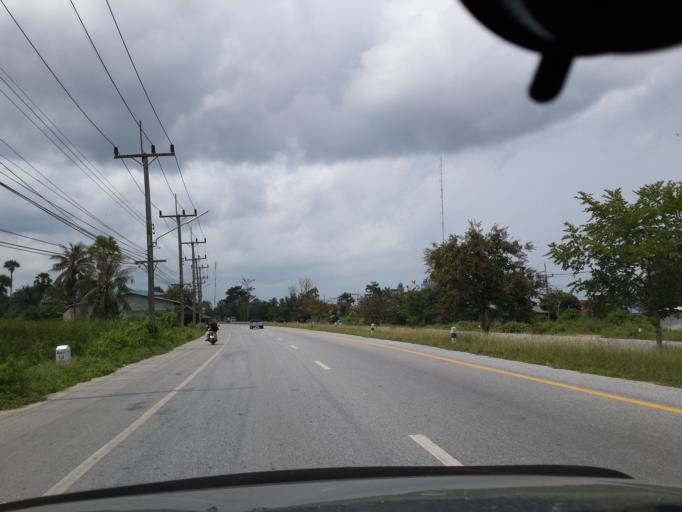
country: TH
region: Pattani
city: Yaring
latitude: 6.8695
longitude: 101.3534
